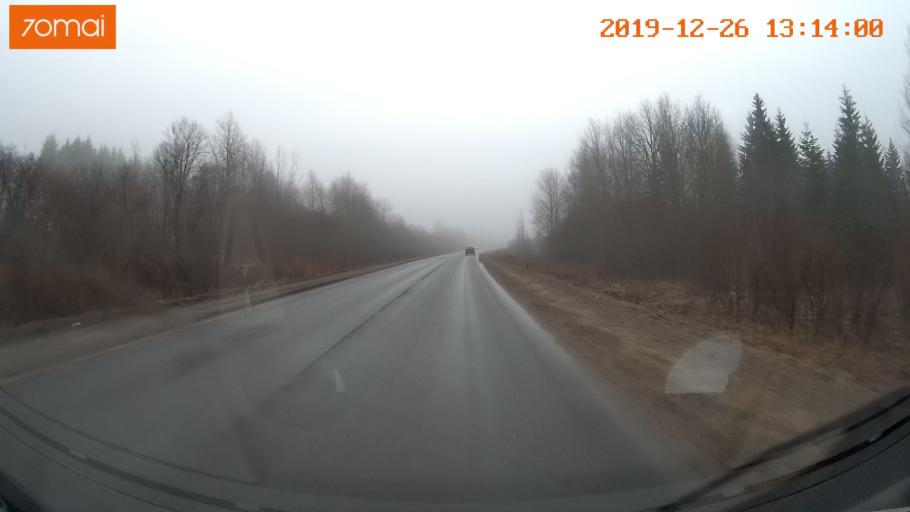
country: RU
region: Vologda
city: Cherepovets
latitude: 59.0133
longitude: 38.0659
